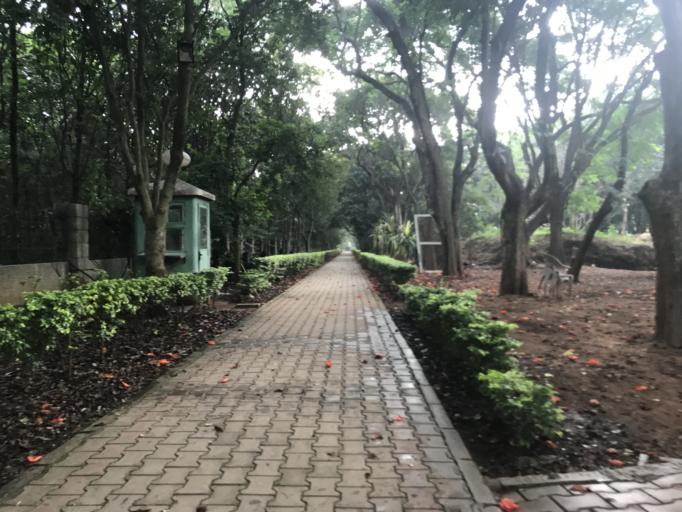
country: IN
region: Karnataka
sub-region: Bangalore Urban
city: Yelahanka
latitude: 13.0726
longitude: 77.5794
